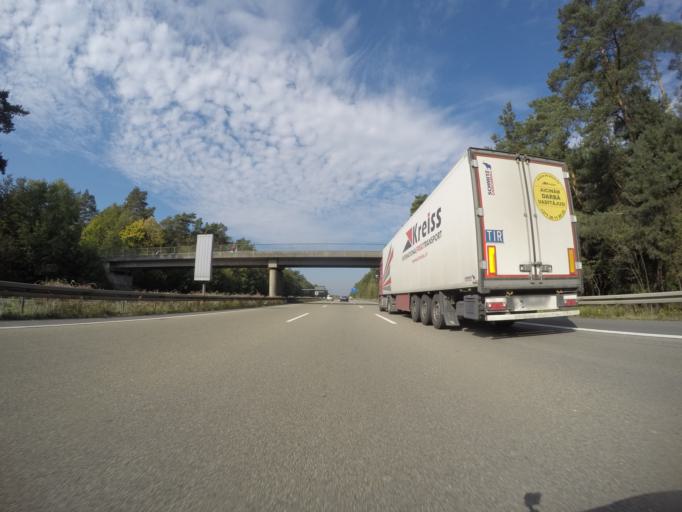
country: DE
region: Hesse
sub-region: Regierungsbezirk Darmstadt
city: Seligenstadt
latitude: 50.0028
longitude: 8.9927
